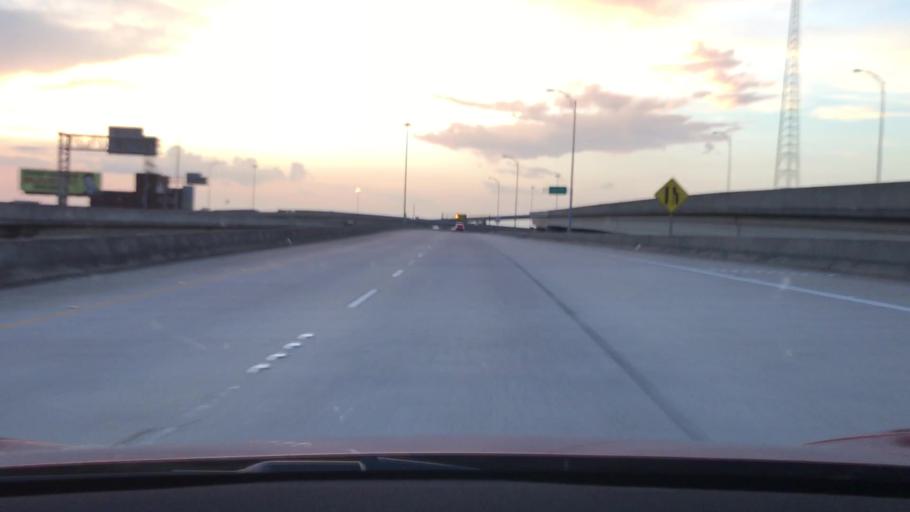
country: US
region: Louisiana
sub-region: Caddo Parish
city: Shreveport
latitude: 32.4927
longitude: -93.7563
